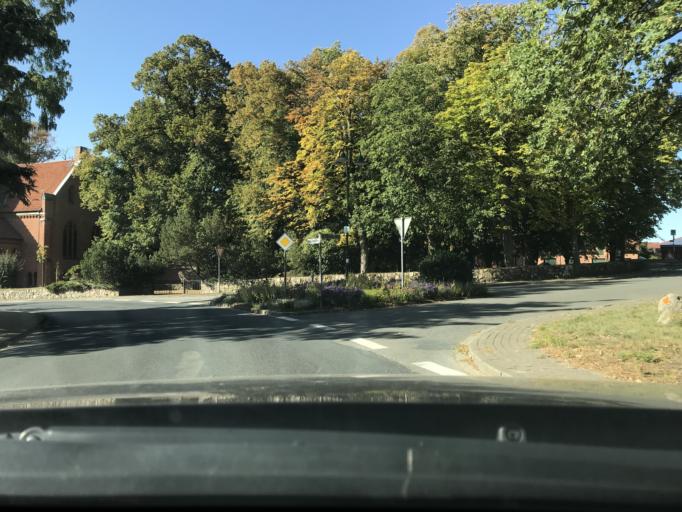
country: DE
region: Lower Saxony
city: Gerdau
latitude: 52.9680
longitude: 10.4196
